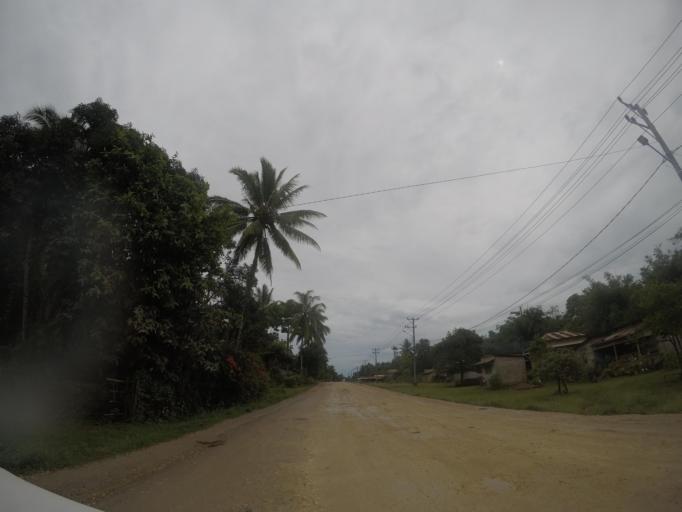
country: TL
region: Lautem
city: Lospalos
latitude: -8.5013
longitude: 126.9901
